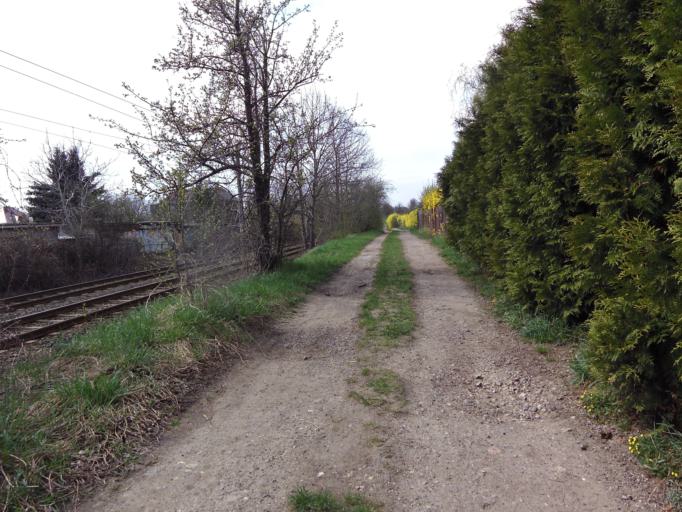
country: DE
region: Saxony
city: Schkeuditz
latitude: 51.3861
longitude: 12.2710
